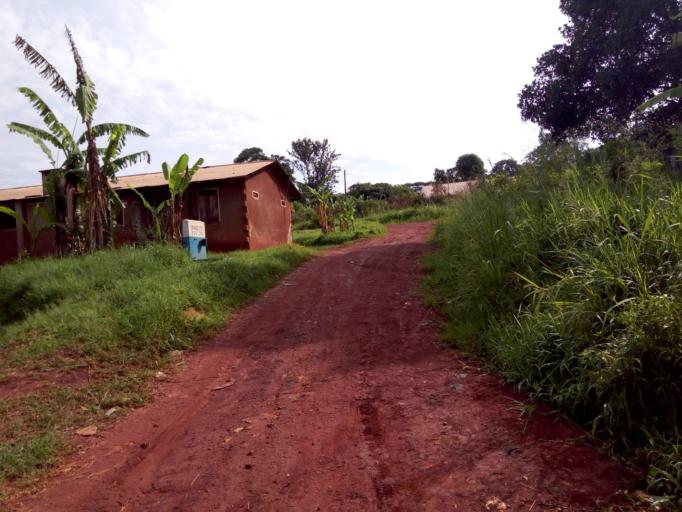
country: UG
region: Western Region
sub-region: Masindi District
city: Masindi
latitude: 1.6870
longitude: 31.7151
